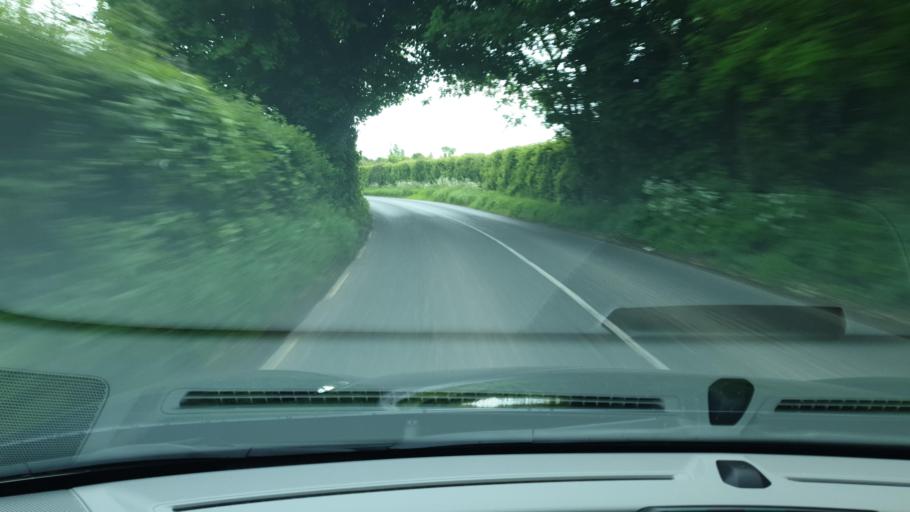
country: IE
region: Leinster
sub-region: An Mhi
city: Ashbourne
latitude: 53.5652
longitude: -6.3607
